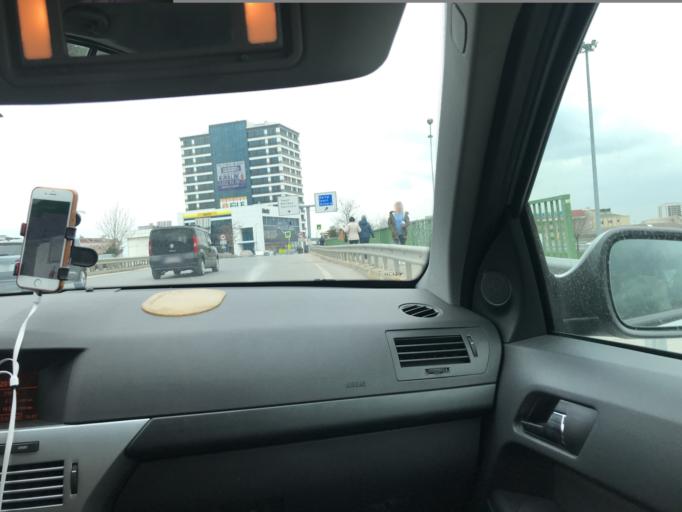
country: TR
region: Istanbul
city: Maltepe
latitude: 40.9258
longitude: 29.1522
